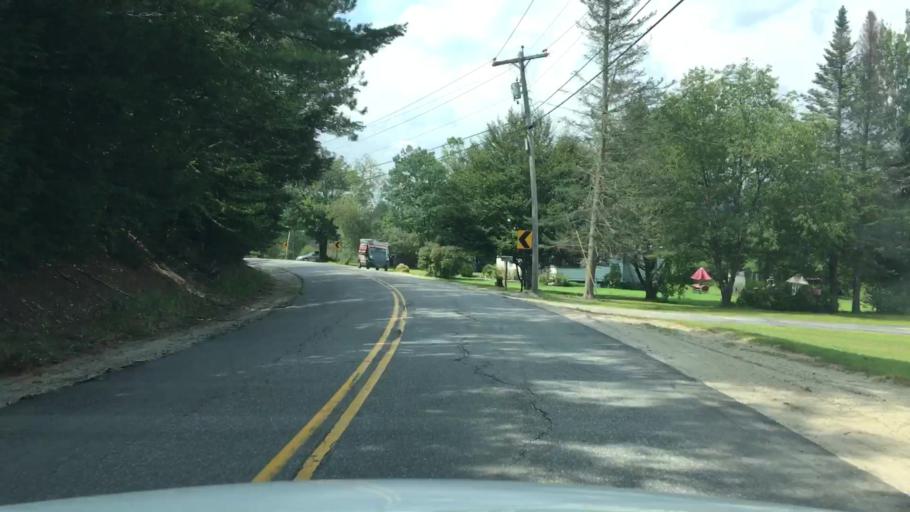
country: US
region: Maine
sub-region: Oxford County
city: Rumford
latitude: 44.5347
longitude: -70.6444
